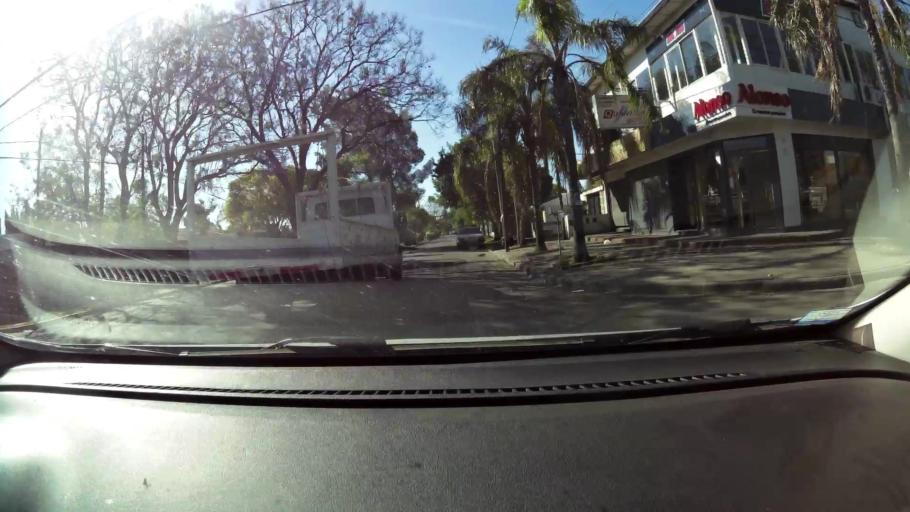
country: AR
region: Cordoba
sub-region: Departamento de Capital
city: Cordoba
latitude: -31.3647
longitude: -64.2018
